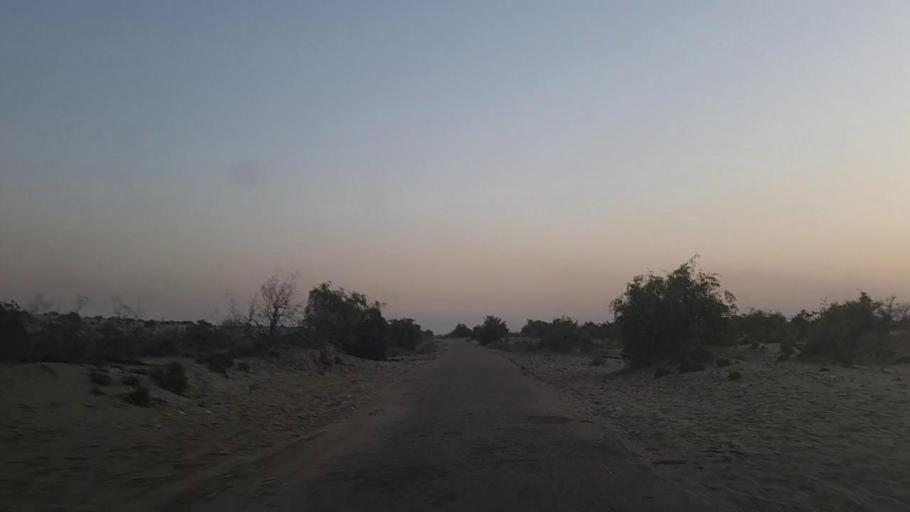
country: PK
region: Sindh
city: Jam Sahib
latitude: 26.3979
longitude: 68.8096
